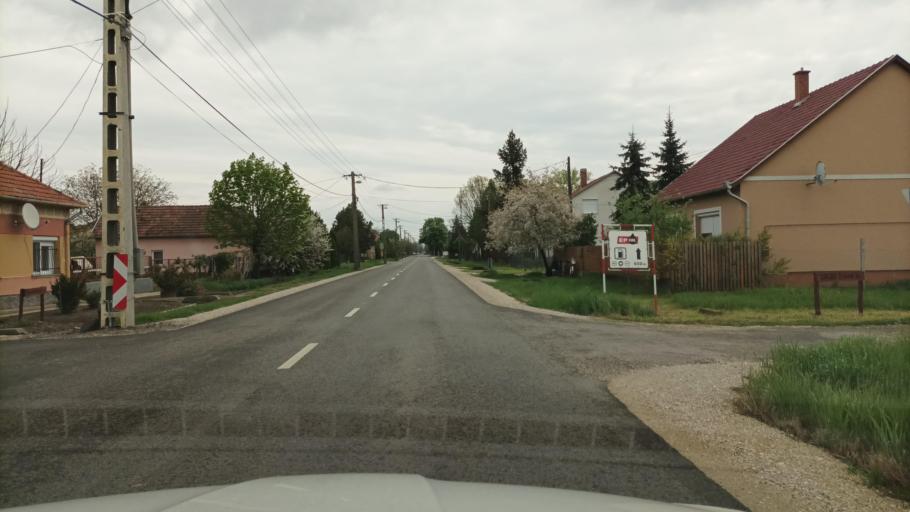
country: HU
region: Pest
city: Kocser
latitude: 47.0047
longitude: 19.9126
